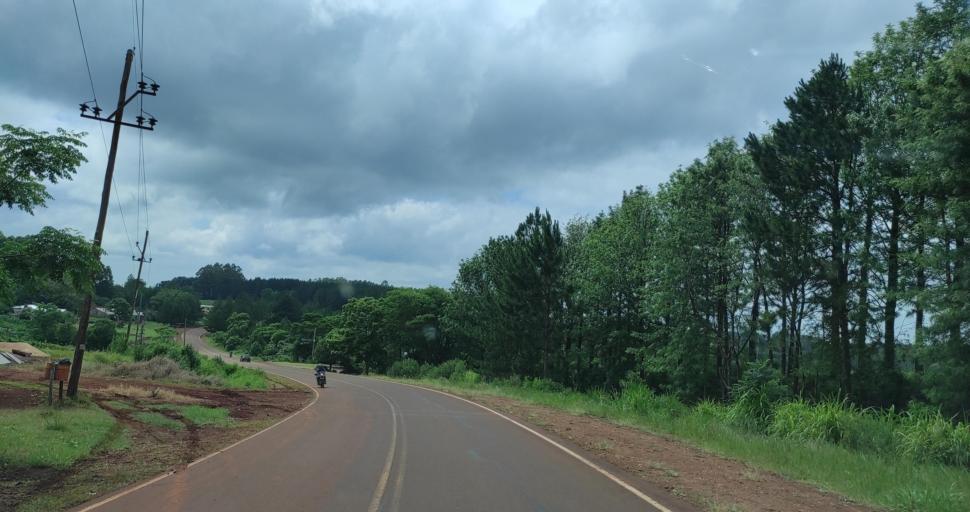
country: AR
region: Misiones
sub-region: Departamento de Veinticinco de Mayo
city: Veinticinco de Mayo
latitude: -27.4108
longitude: -54.7443
